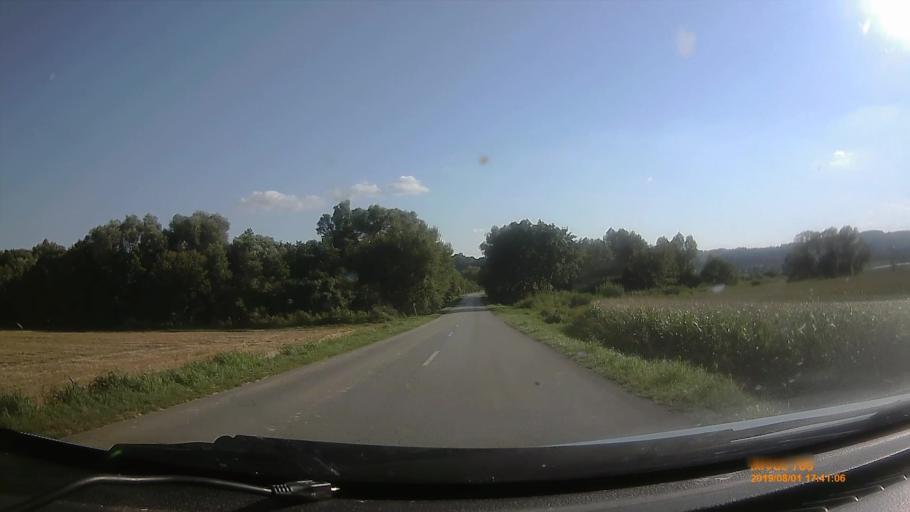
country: HU
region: Baranya
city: Komlo
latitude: 46.1953
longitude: 18.1782
